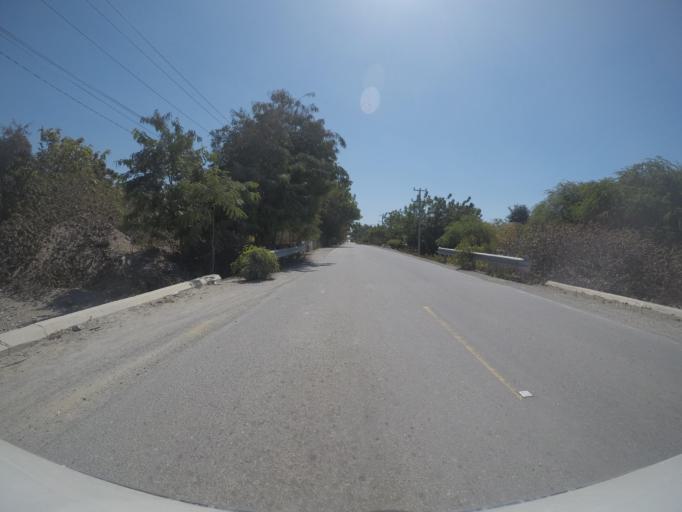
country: TL
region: Liquica
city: Liquica
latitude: -8.5677
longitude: 125.4313
